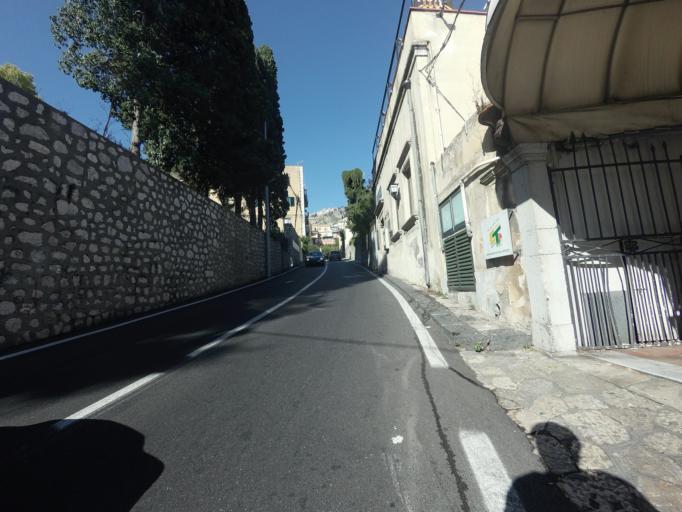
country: IT
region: Sicily
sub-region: Messina
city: Taormina
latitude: 37.8553
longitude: 15.2905
